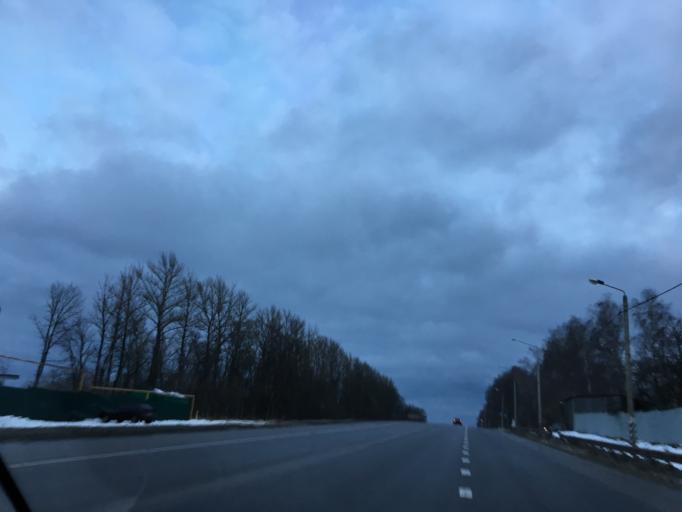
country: RU
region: Tula
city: Barsuki
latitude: 54.3481
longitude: 37.5401
